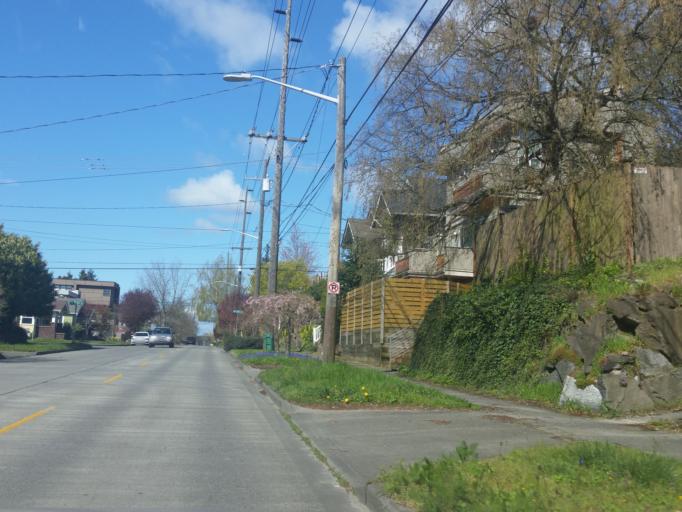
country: US
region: Washington
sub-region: King County
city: Shoreline
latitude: 47.6827
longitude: -122.3607
